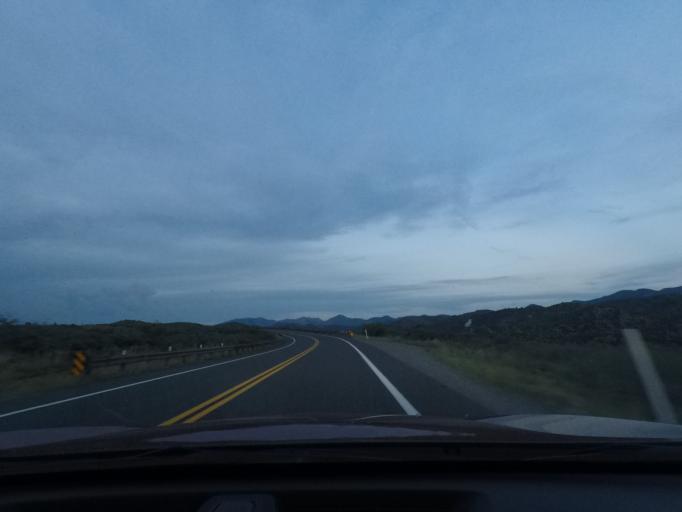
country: US
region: Arizona
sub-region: Yavapai County
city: Williamson
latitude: 34.5520
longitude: -112.6720
